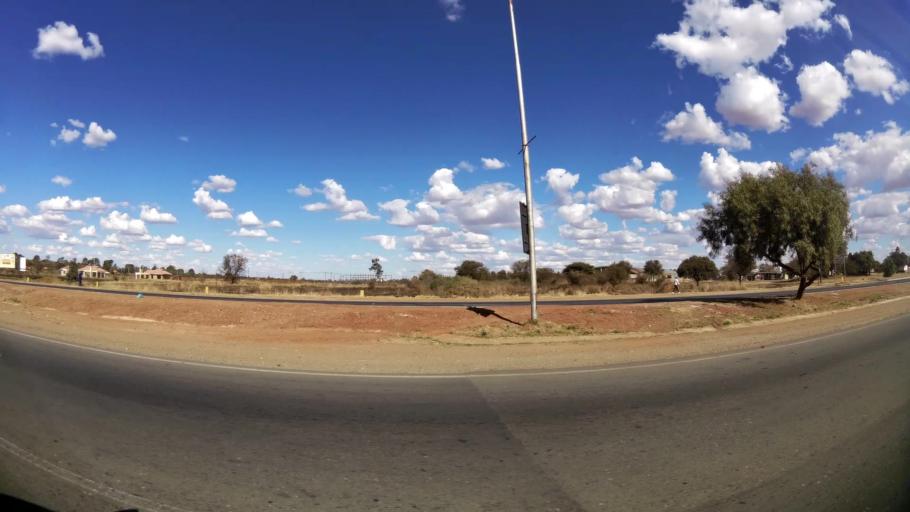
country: ZA
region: North-West
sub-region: Dr Kenneth Kaunda District Municipality
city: Klerksdorp
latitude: -26.8680
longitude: 26.6289
